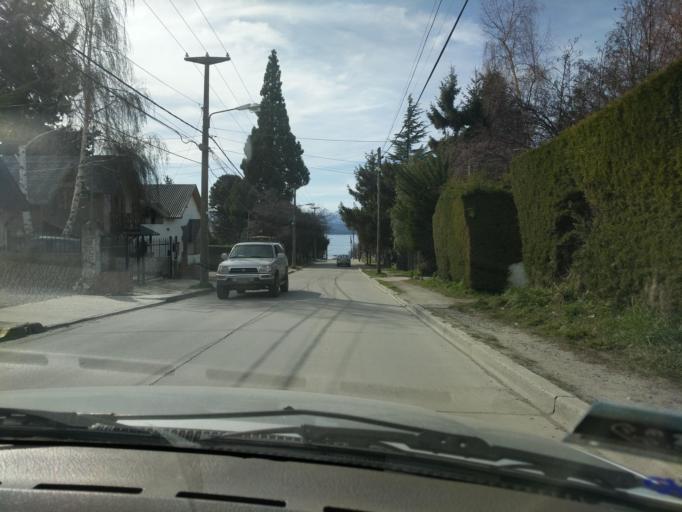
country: AR
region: Rio Negro
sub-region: Departamento de Bariloche
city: San Carlos de Bariloche
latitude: -41.1288
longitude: -71.3555
